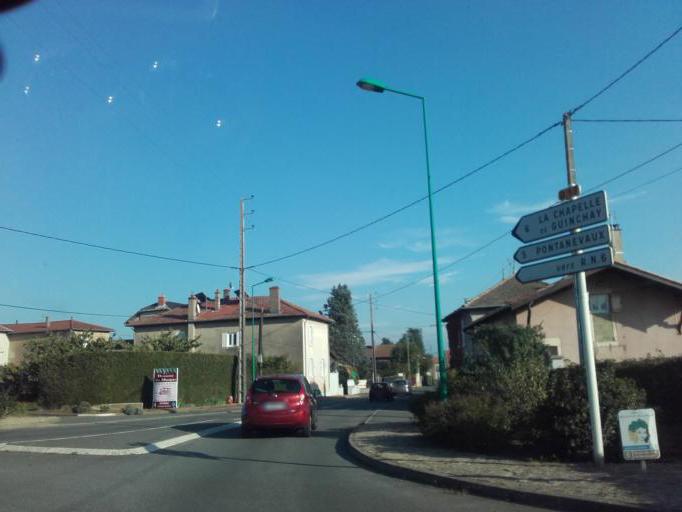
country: FR
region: Rhone-Alpes
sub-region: Departement du Rhone
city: Fleurie
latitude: 46.2296
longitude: 4.7213
